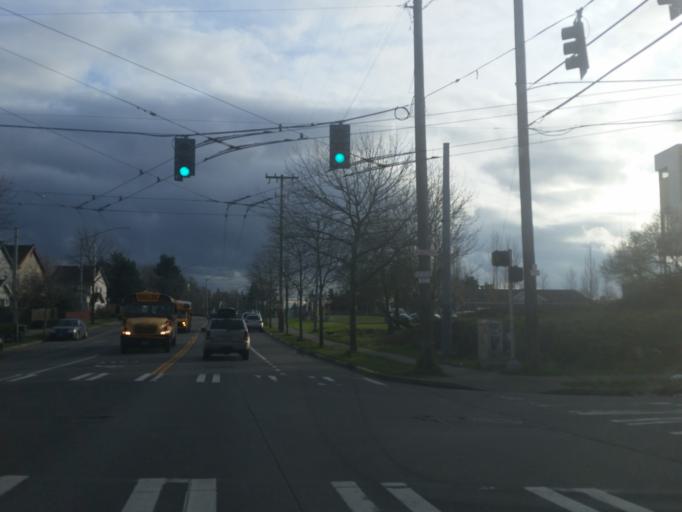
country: US
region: Washington
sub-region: King County
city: Seattle
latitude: 47.5921
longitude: -122.2978
